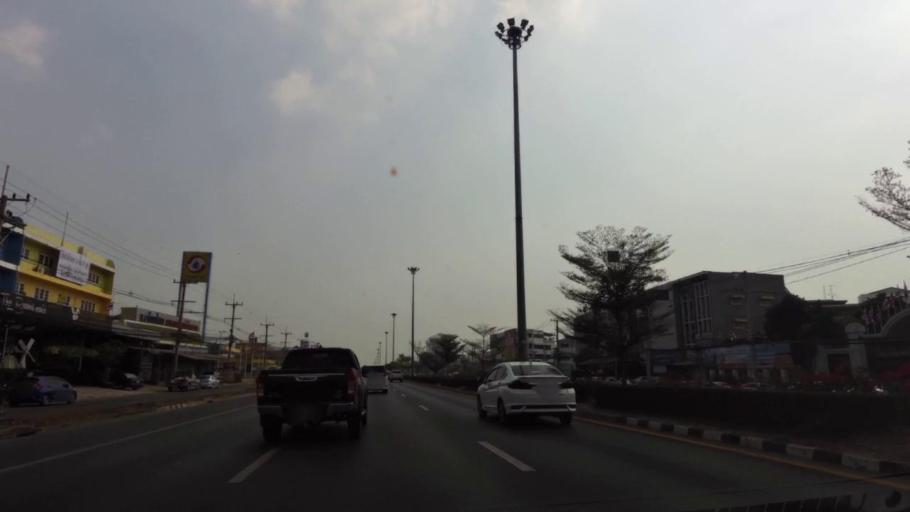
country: TH
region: Phra Nakhon Si Ayutthaya
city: Phra Nakhon Si Ayutthaya
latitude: 14.3508
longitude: 100.6025
